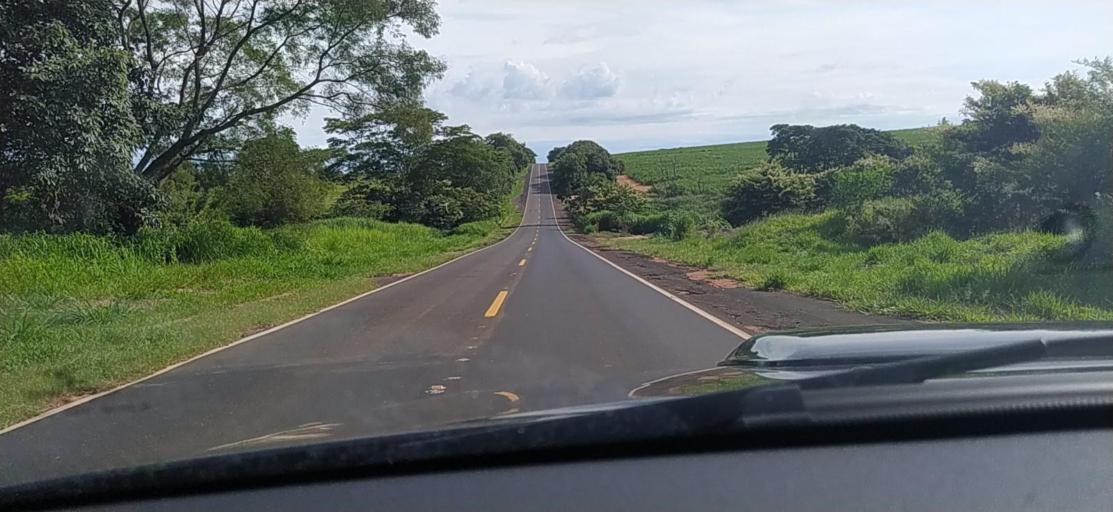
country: BR
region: Sao Paulo
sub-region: Catanduva
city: Catanduva
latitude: -21.0845
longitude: -49.0733
